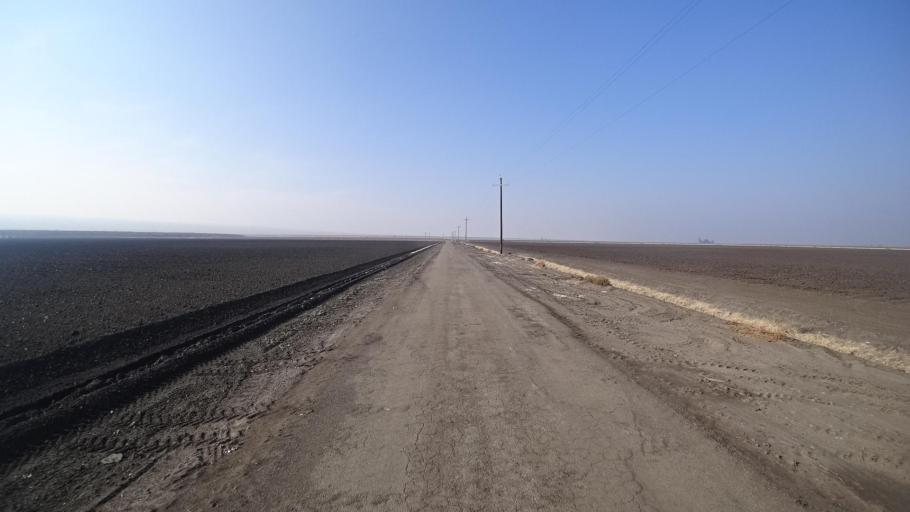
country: US
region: California
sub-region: Kern County
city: Buttonwillow
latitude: 35.3545
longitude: -119.4524
